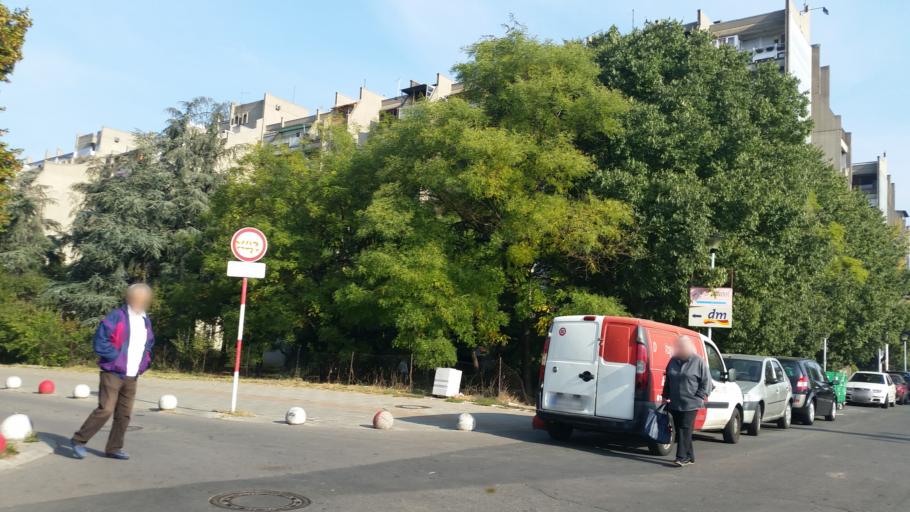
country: RS
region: Central Serbia
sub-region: Belgrade
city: Novi Beograd
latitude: 44.8098
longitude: 20.4297
